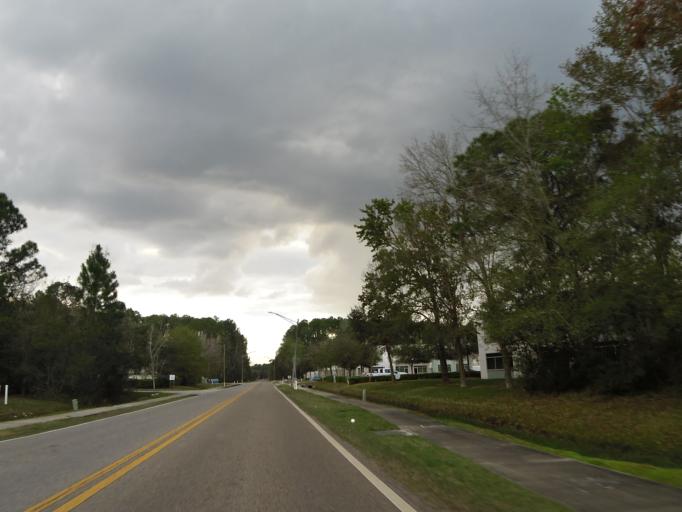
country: US
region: Florida
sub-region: Saint Johns County
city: Fruit Cove
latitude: 30.1879
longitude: -81.5744
